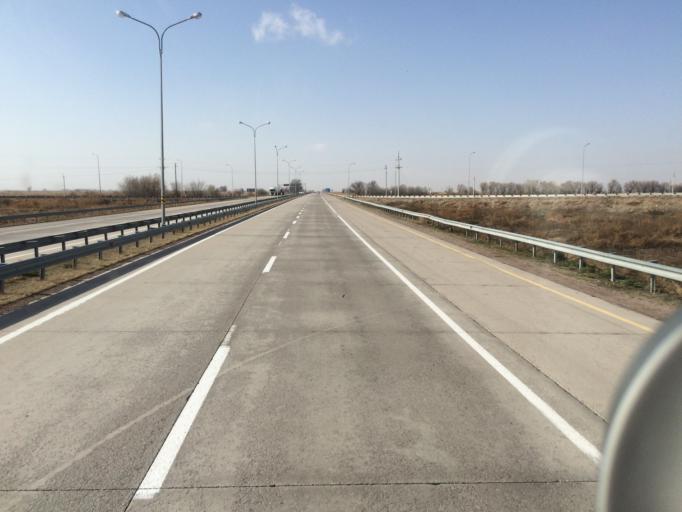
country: KZ
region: Zhambyl
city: Oytal
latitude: 42.9287
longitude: 73.2416
